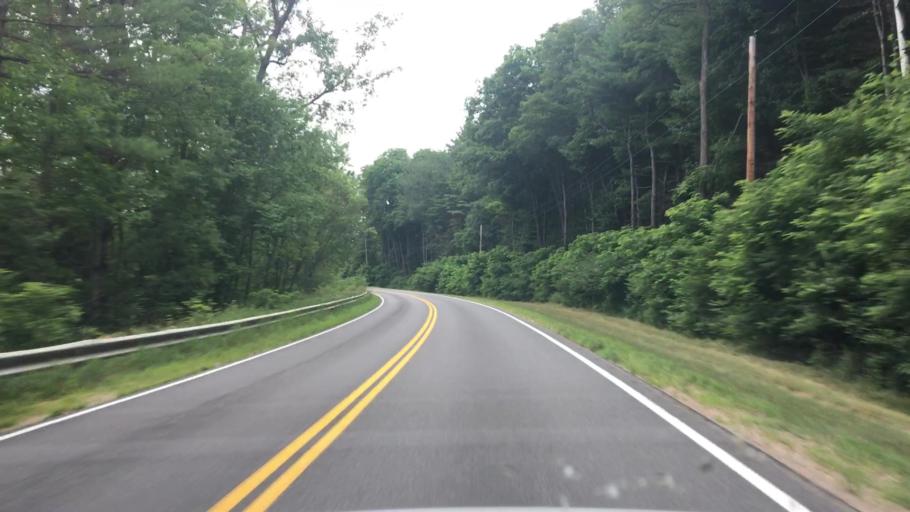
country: US
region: New York
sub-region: Clinton County
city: Morrisonville
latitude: 44.6152
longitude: -73.6330
